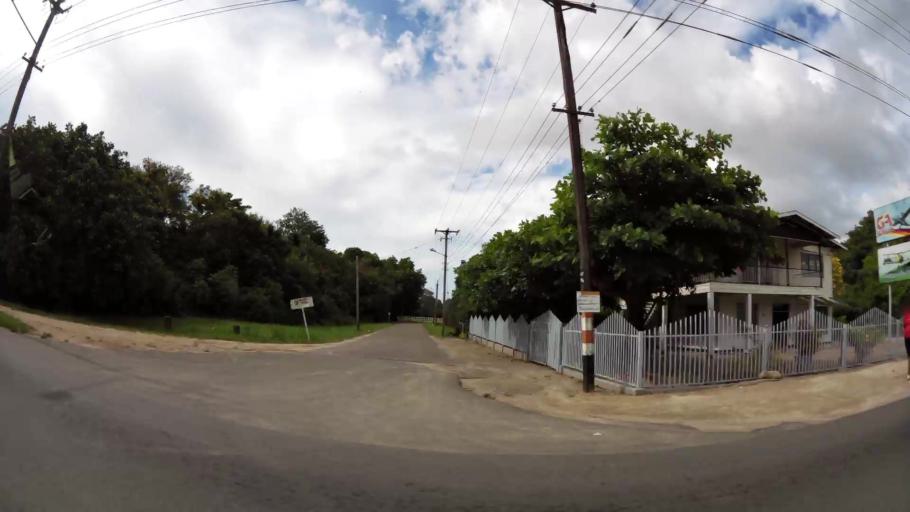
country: SR
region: Paramaribo
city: Paramaribo
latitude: 5.8411
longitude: -55.1894
